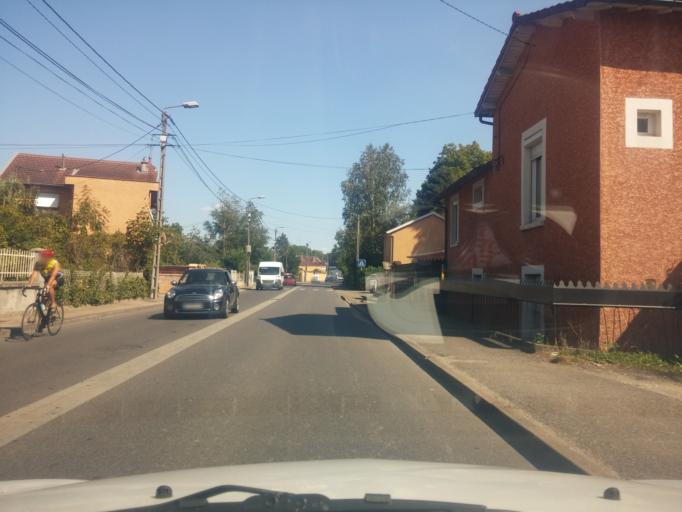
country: FR
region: Rhone-Alpes
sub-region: Departement du Rhone
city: Sainte-Foy-les-Lyon
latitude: 45.7225
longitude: 4.7855
